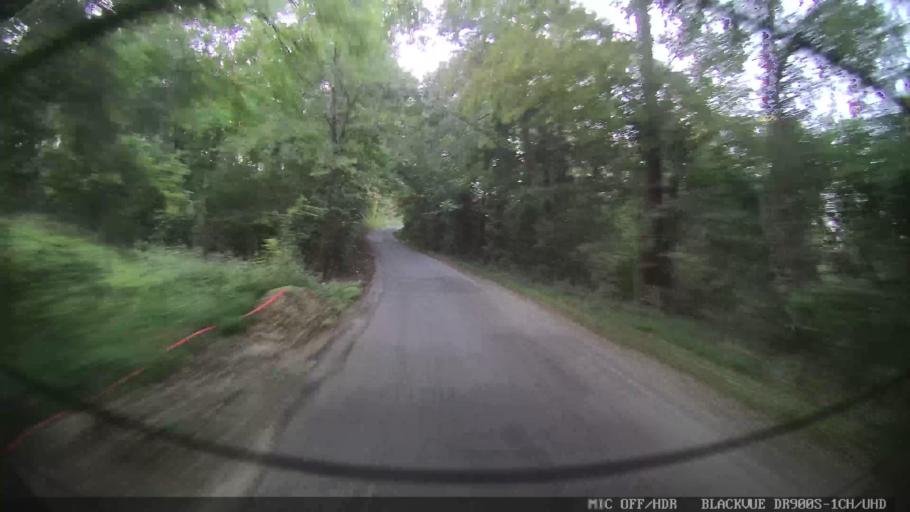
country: US
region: Tennessee
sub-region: Bradley County
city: Wildwood Lake
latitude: 35.0144
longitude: -84.7480
